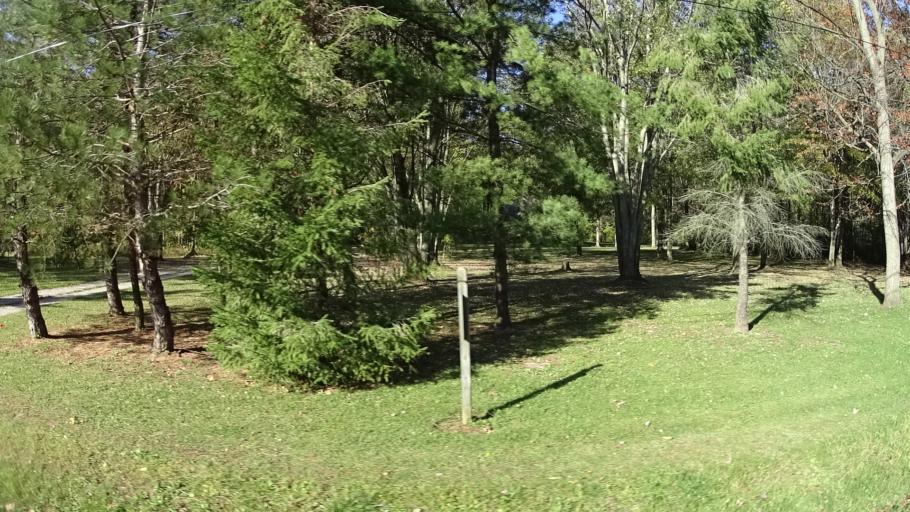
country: US
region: Ohio
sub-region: Lorain County
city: South Amherst
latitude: 41.3760
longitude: -82.2977
